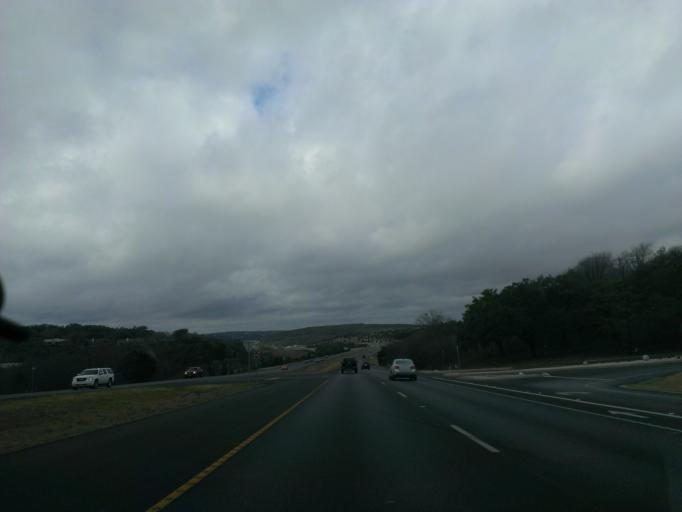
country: US
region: Texas
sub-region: Williamson County
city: Jollyville
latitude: 30.3885
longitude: -97.7509
